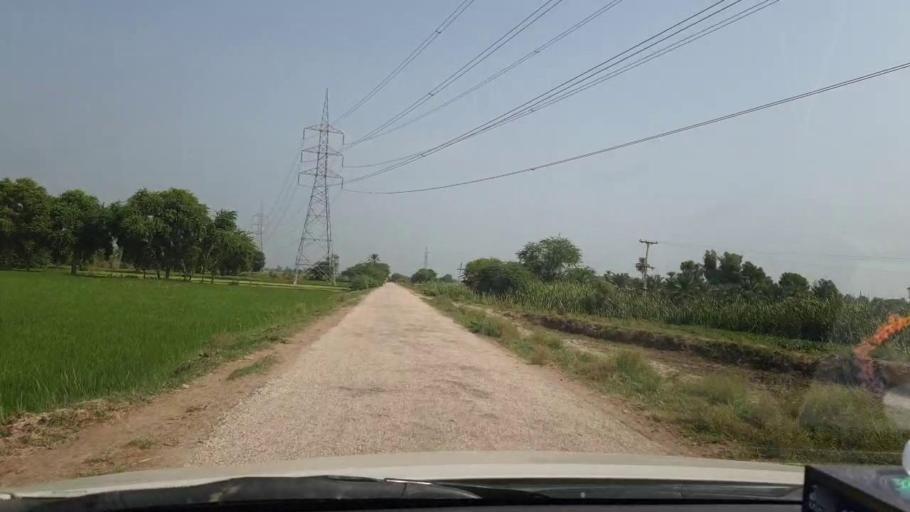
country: PK
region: Sindh
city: Shikarpur
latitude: 27.9777
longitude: 68.6643
